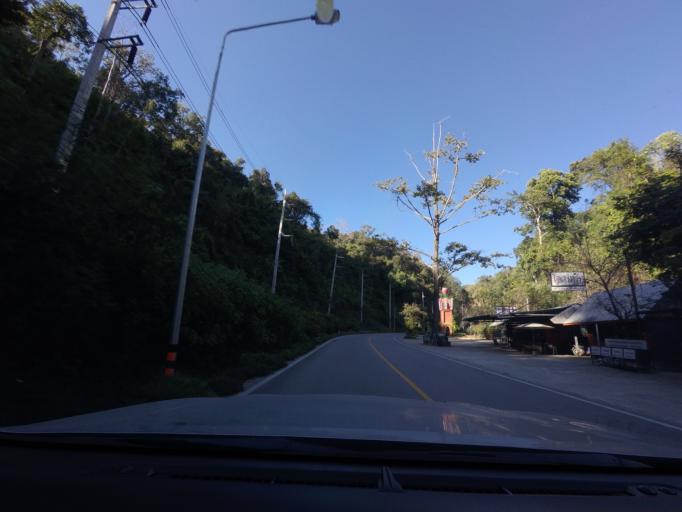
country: TH
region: Mae Hong Son
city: Mae Hi
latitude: 19.2085
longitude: 98.6703
